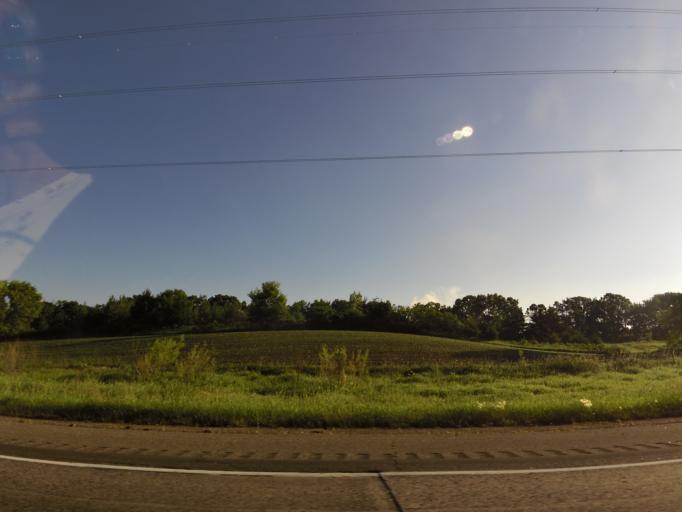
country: US
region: Minnesota
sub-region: Sherburne County
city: Becker
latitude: 45.3529
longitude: -93.9146
